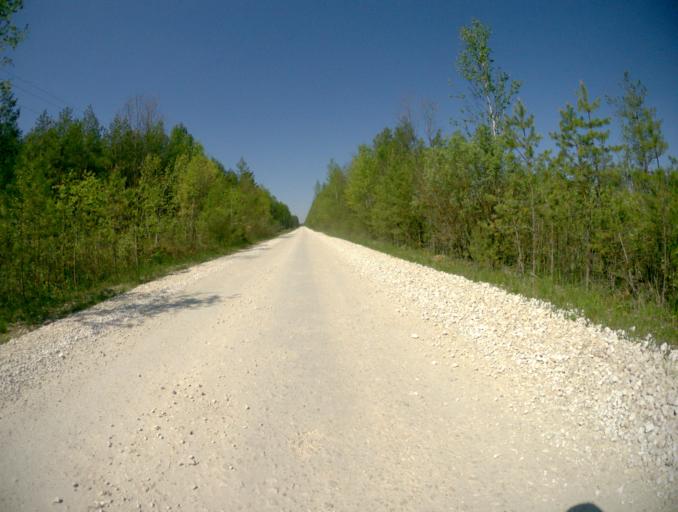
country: RU
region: Vladimir
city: Anopino
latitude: 55.7195
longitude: 40.6018
